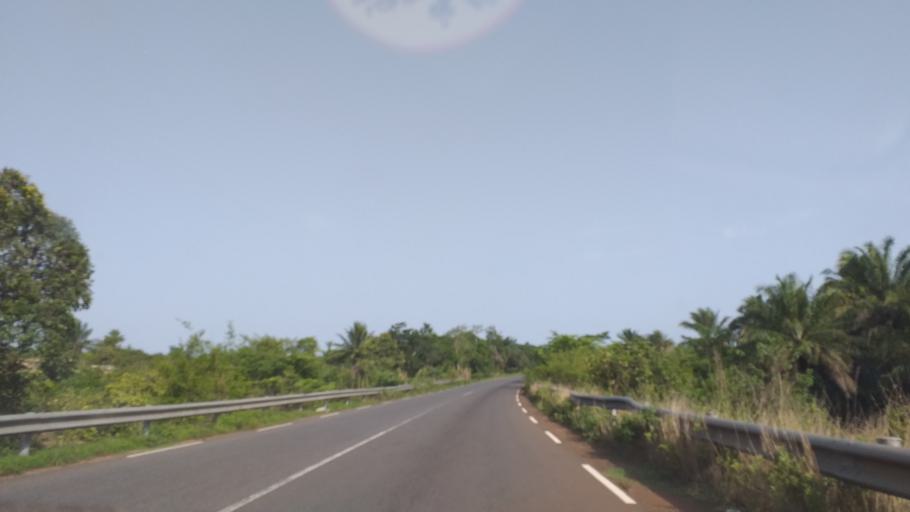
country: GN
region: Boke
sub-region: Boffa
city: Boffa
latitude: 10.2915
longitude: -14.1912
